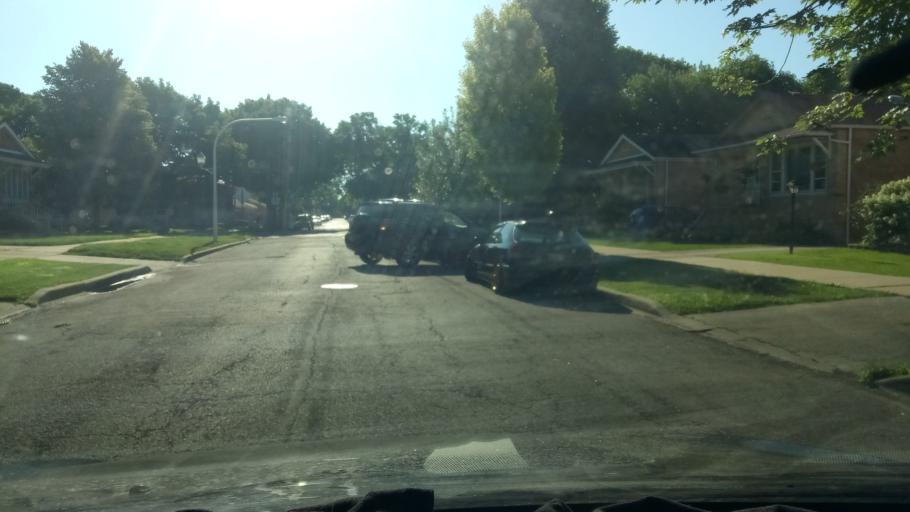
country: US
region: Illinois
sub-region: Cook County
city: Hometown
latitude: 41.7730
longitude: -87.7357
